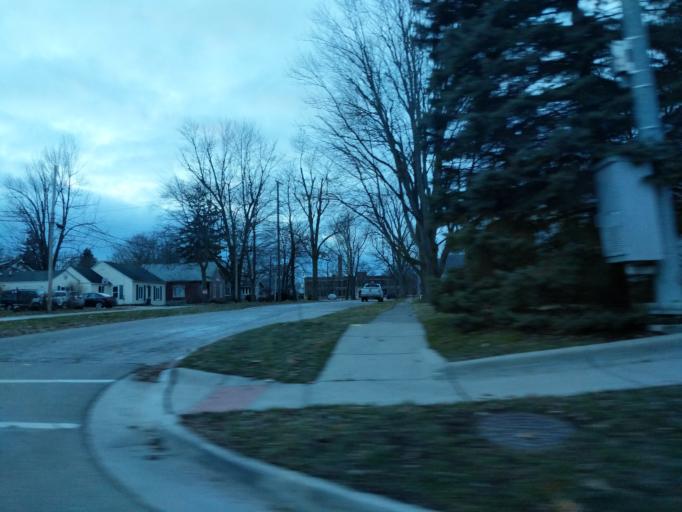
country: US
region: Michigan
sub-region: Lapeer County
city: Almont
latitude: 42.9233
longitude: -83.0453
